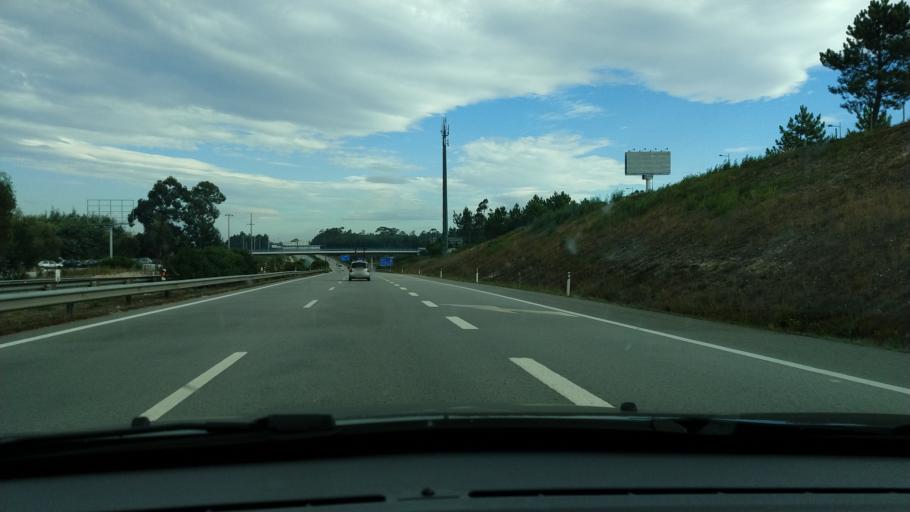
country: PT
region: Aveiro
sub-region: Aveiro
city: Eixo
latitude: 40.6504
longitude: -8.5951
